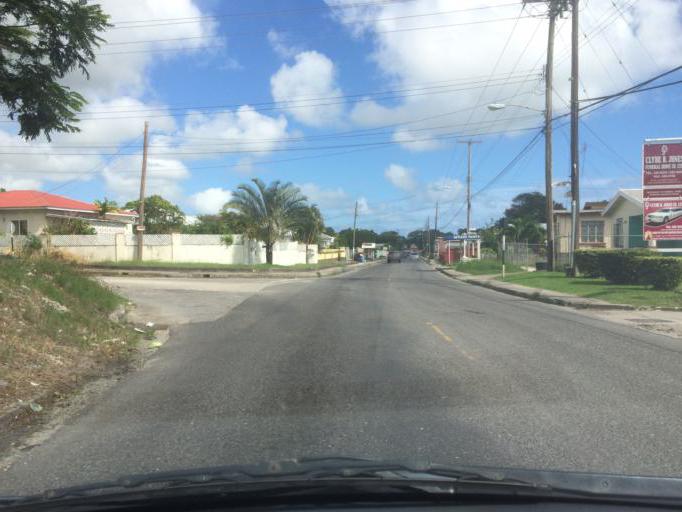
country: BB
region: Christ Church
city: Oistins
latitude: 13.0701
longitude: -59.5664
